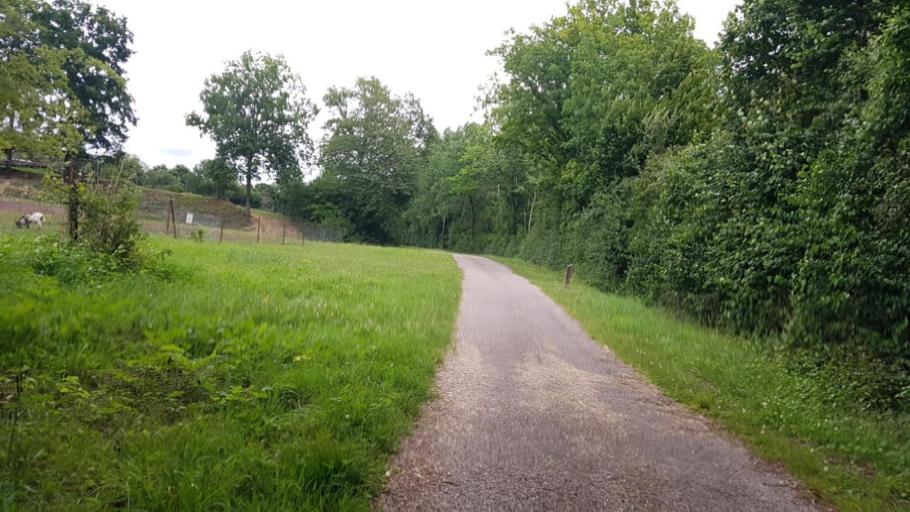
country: FR
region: Picardie
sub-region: Departement de l'Aisne
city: Origny-en-Thierache
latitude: 49.9272
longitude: 3.9897
